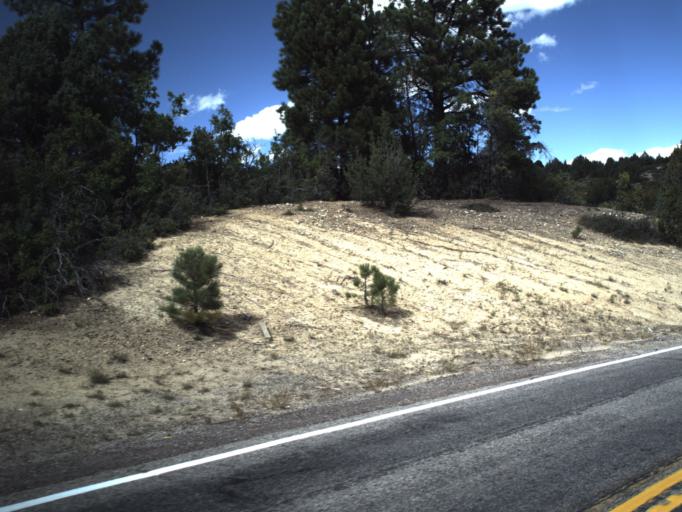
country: US
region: Utah
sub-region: Garfield County
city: Panguitch
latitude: 37.4909
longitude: -112.5236
